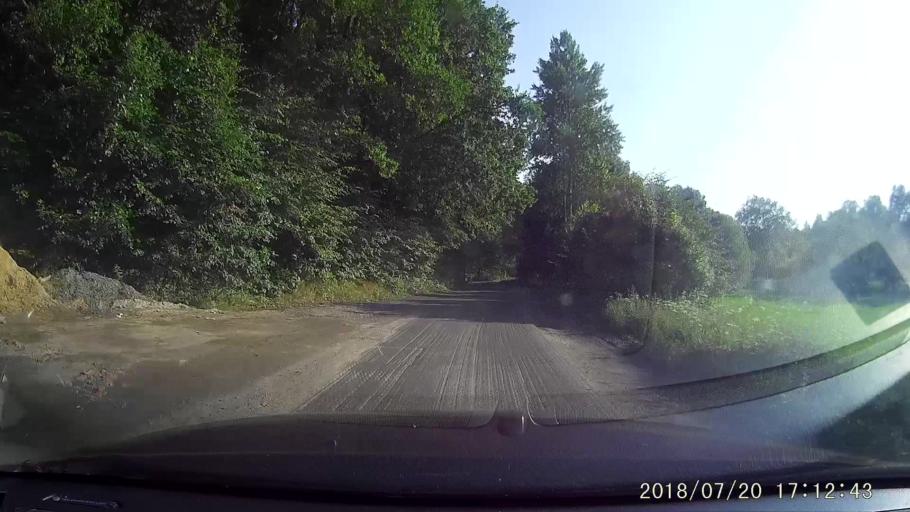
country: PL
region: Lower Silesian Voivodeship
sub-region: Powiat lubanski
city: Lesna
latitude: 51.0180
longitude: 15.2751
